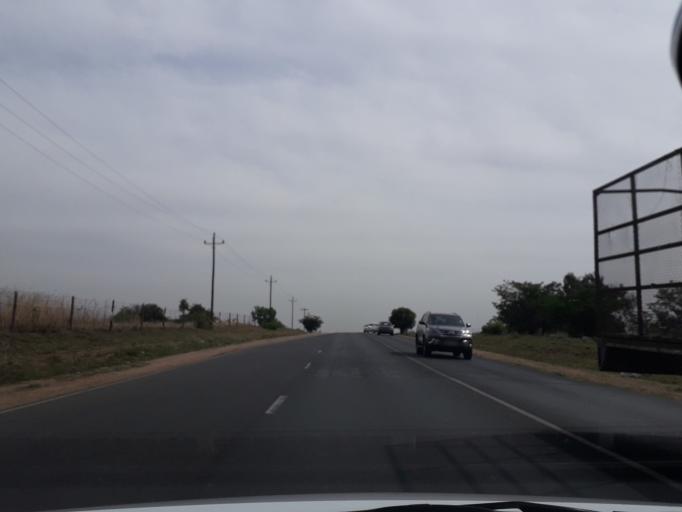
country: ZA
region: Gauteng
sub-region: City of Johannesburg Metropolitan Municipality
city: Diepsloot
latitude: -25.9940
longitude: 28.0483
